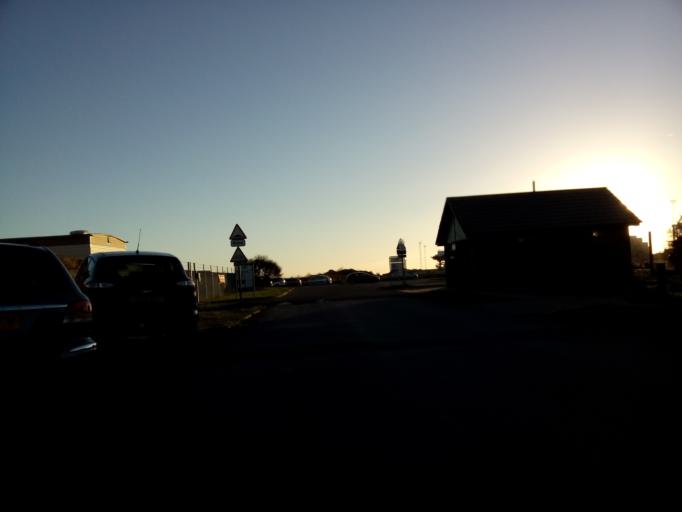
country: GB
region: England
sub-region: Suffolk
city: Felixstowe
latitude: 51.9448
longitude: 1.3309
